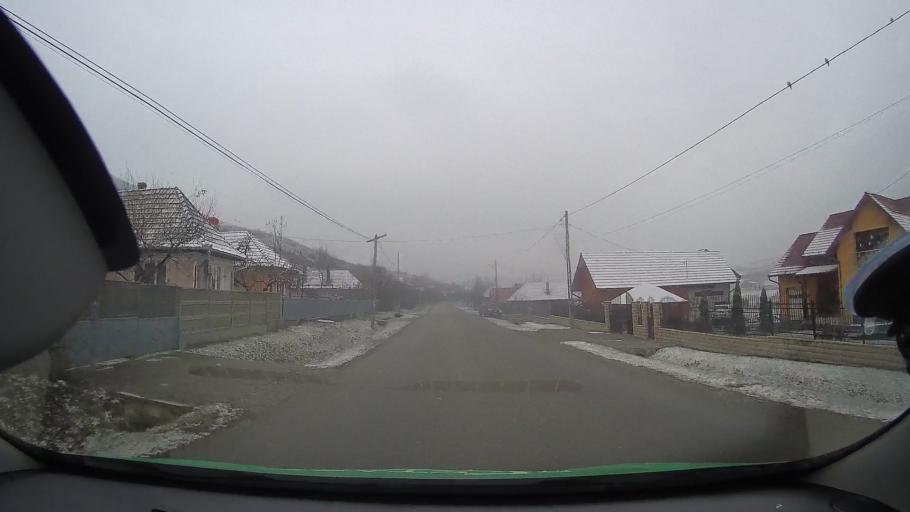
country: RO
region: Alba
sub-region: Comuna Noslac
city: Noslac
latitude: 46.3493
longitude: 23.9373
